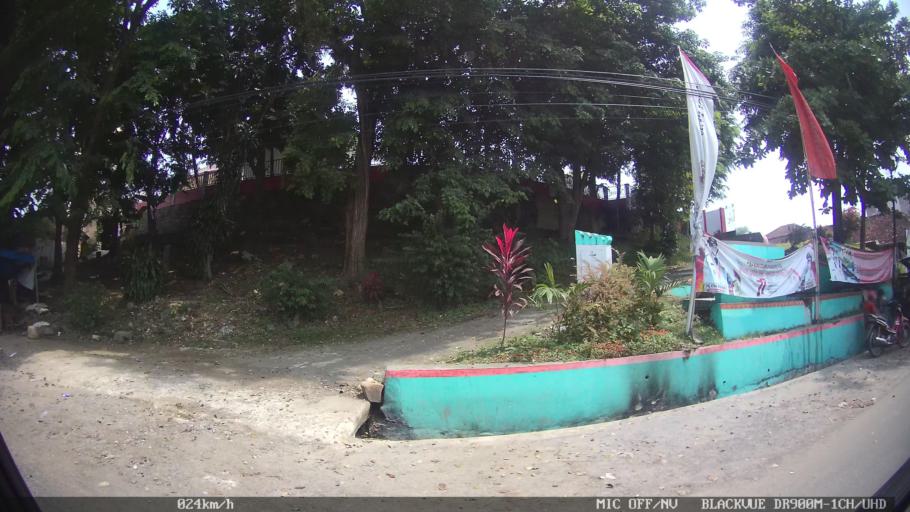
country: ID
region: Lampung
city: Bandarlampung
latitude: -5.4520
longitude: 105.2513
